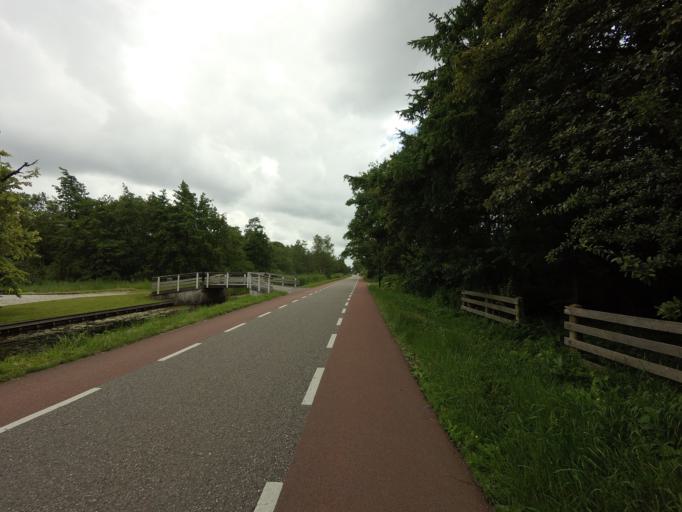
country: NL
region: North Holland
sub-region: Gemeente Wijdemeren
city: Oud-Loosdrecht
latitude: 52.2208
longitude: 5.0746
